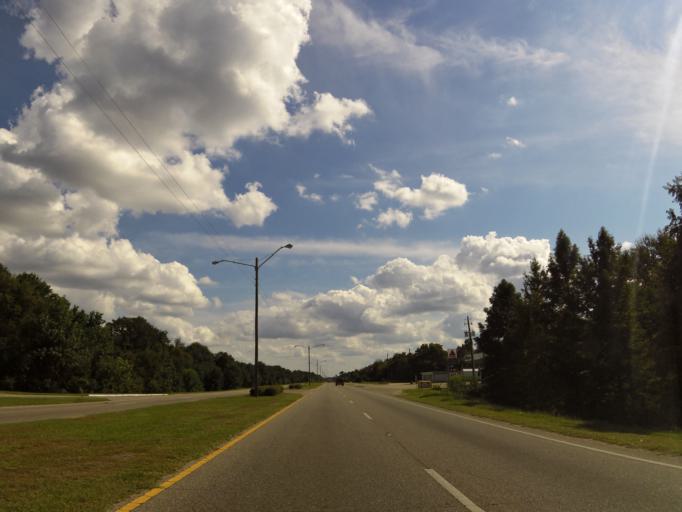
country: US
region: Alabama
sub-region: Dallas County
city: Selma
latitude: 32.3972
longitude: -87.0152
